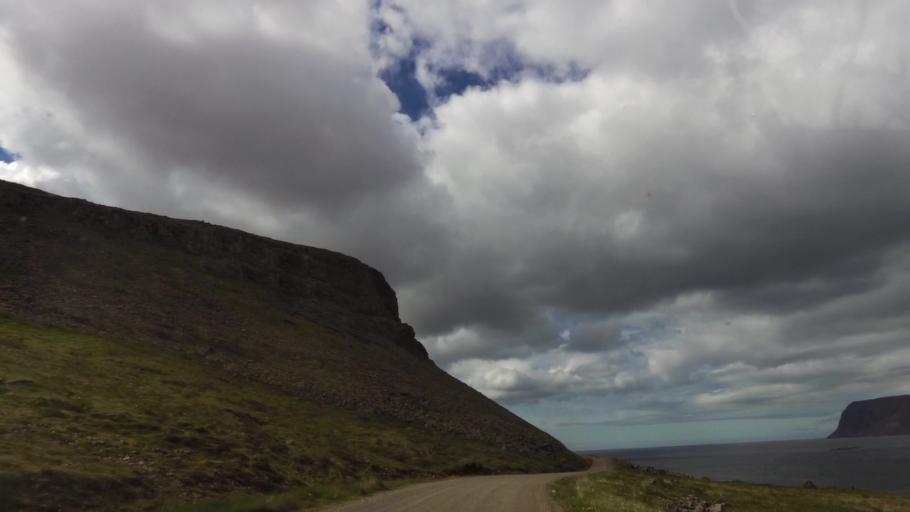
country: IS
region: West
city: Olafsvik
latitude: 65.5617
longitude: -24.0344
